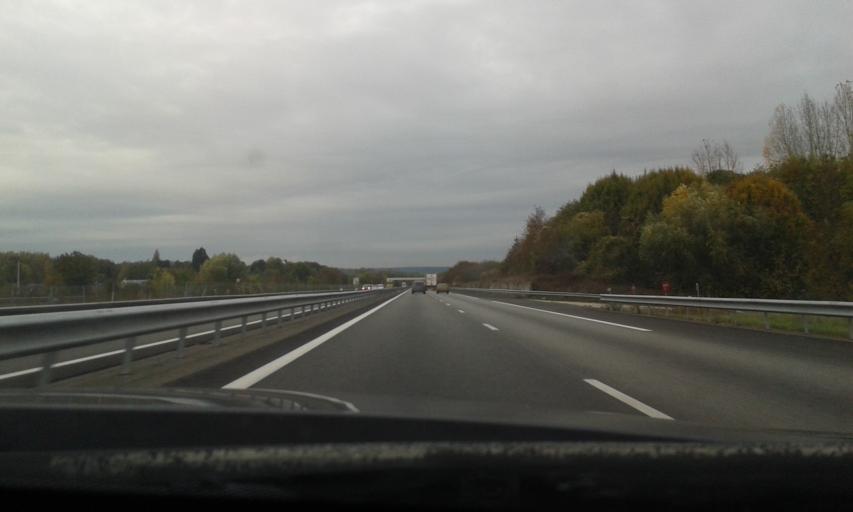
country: FR
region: Haute-Normandie
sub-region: Departement de l'Eure
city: Louviers
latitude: 49.2147
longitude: 1.1812
